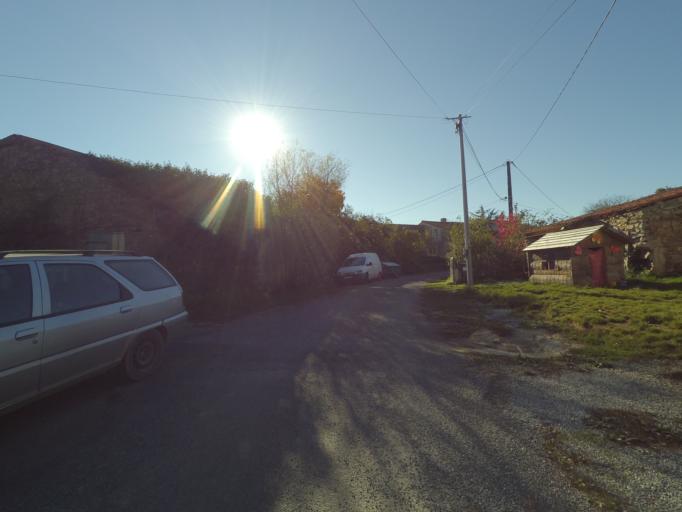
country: FR
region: Pays de la Loire
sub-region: Departement de la Vendee
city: Saint-Hilaire-de-Loulay
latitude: 46.9996
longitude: -1.3739
